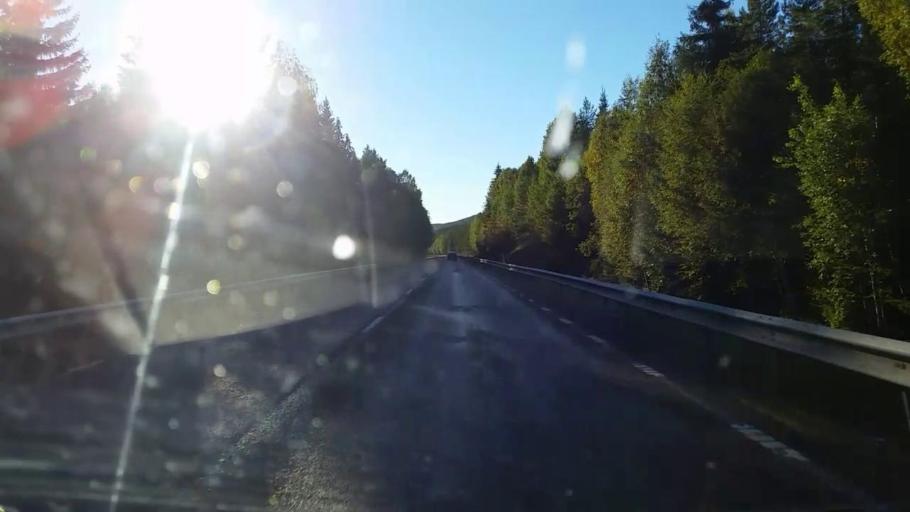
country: SE
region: Gaevleborg
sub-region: Hudiksvalls Kommun
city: Delsbo
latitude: 61.8071
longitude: 16.4171
